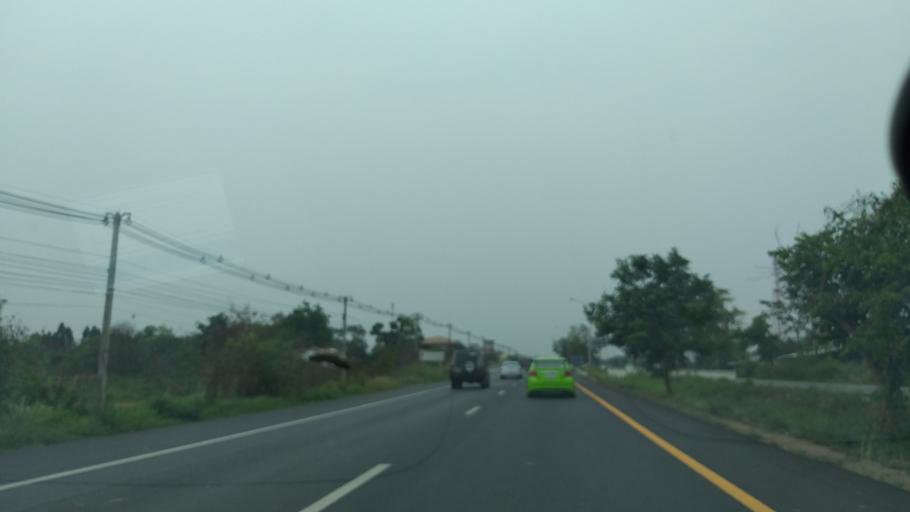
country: TH
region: Chon Buri
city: Ko Chan
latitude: 13.3744
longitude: 101.2761
